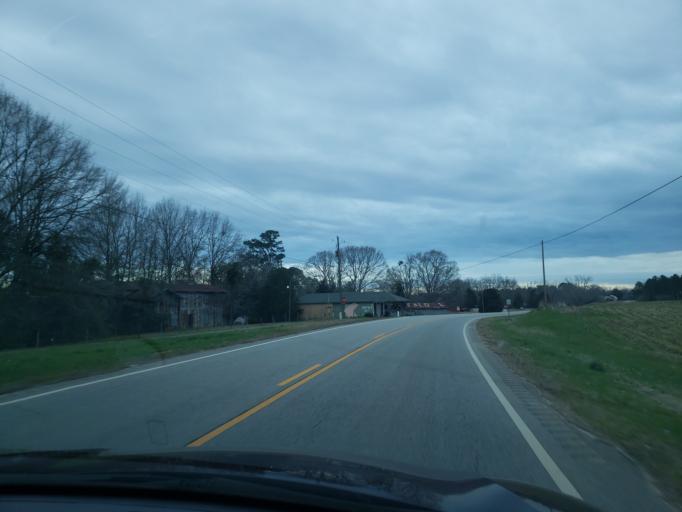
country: US
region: Alabama
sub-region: Chambers County
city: Lafayette
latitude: 32.9478
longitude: -85.4023
